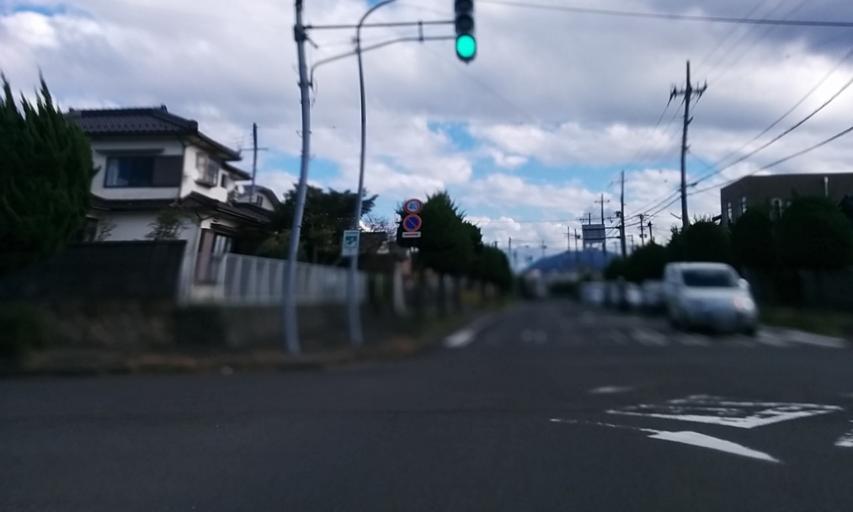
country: JP
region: Fukui
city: Obama
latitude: 35.5002
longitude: 135.7420
